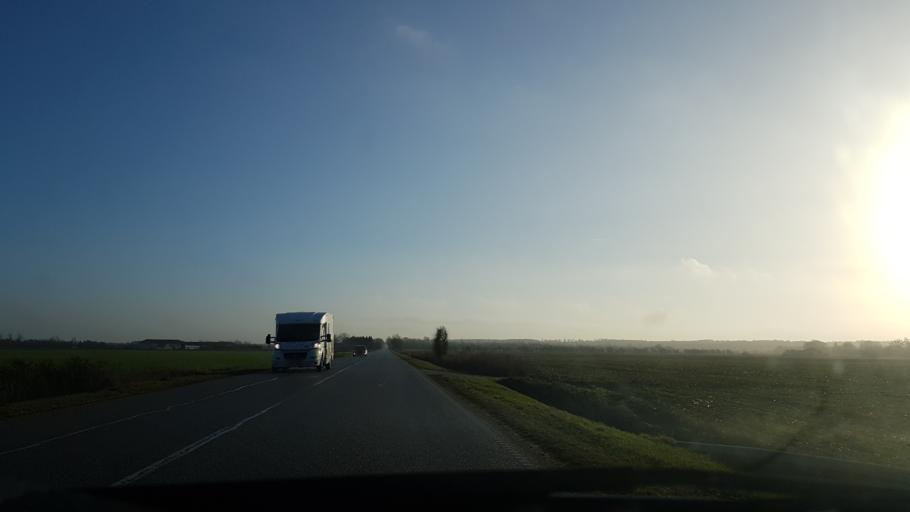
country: DK
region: South Denmark
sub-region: Tonder Kommune
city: Toftlund
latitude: 55.2438
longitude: 9.1562
